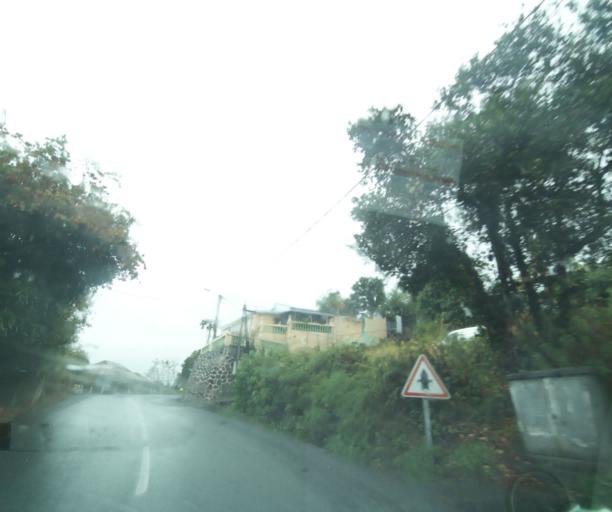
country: RE
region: Reunion
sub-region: Reunion
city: Saint-Paul
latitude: -21.0209
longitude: 55.2988
